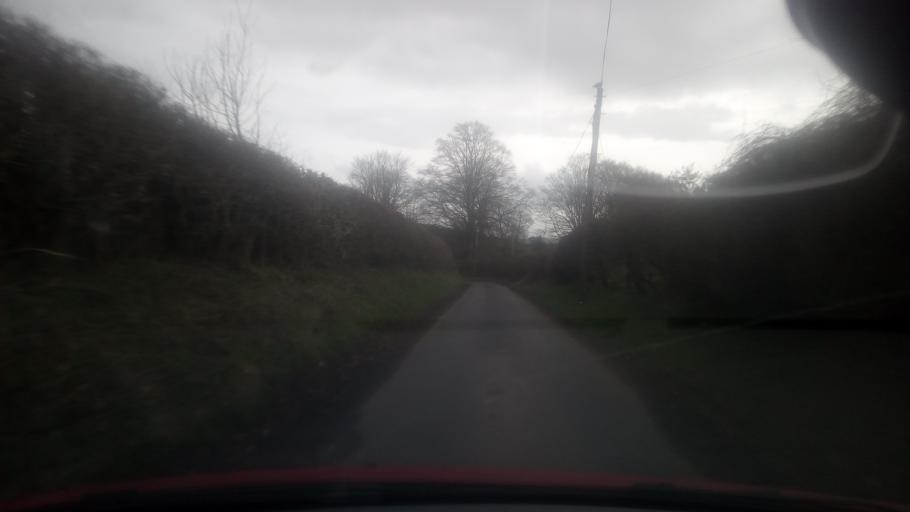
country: GB
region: Scotland
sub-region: The Scottish Borders
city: Jedburgh
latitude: 55.4750
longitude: -2.5404
